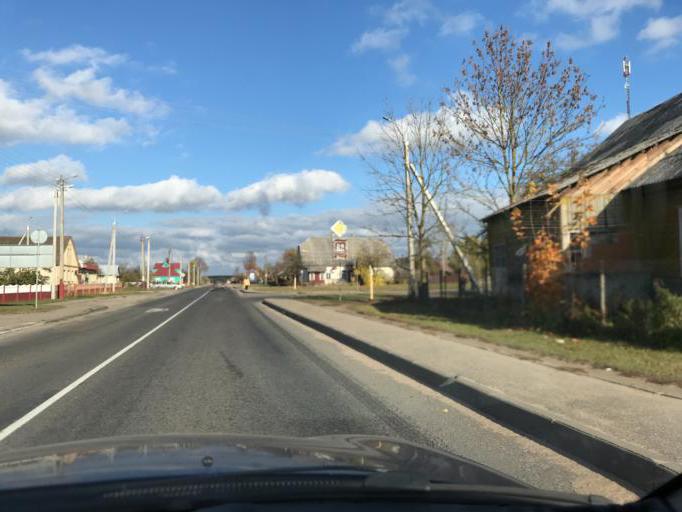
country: LT
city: Salcininkai
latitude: 54.2523
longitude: 25.3564
